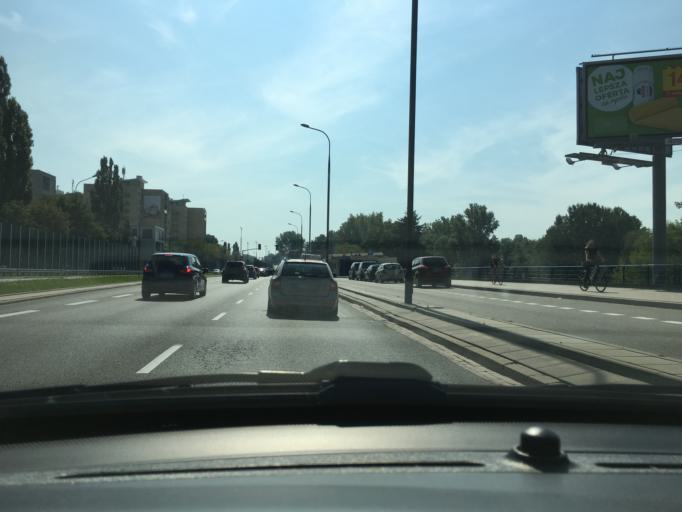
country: PL
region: Masovian Voivodeship
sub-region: Warszawa
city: Praga Polnoc
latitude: 52.2314
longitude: 21.0494
